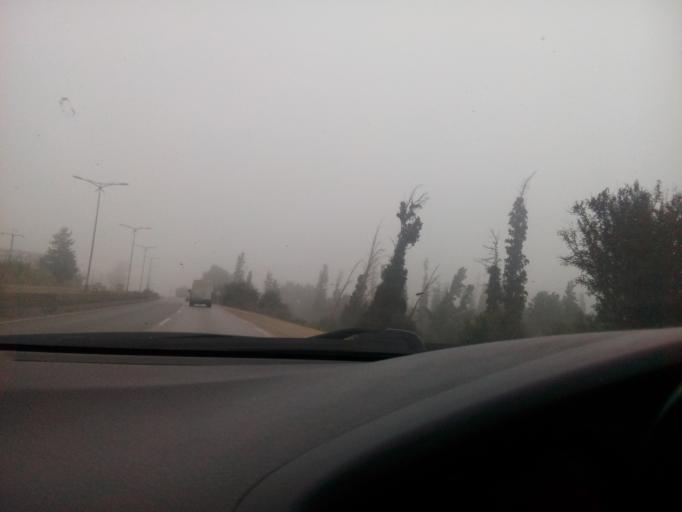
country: DZ
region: Oran
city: Bou Tlelis
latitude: 35.5734
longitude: -0.8582
